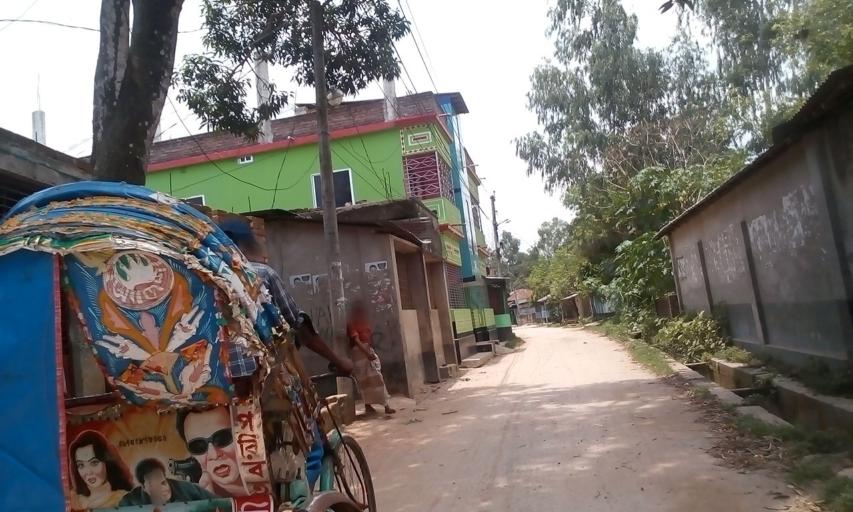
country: IN
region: West Bengal
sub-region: Dakshin Dinajpur
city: Balurghat
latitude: 25.3907
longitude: 88.9876
